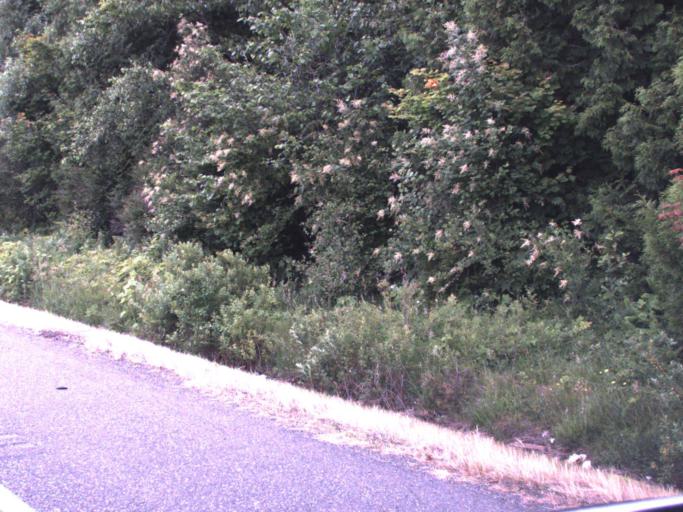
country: US
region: Washington
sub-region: Whatcom County
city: Birch Bay
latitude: 48.8921
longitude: -122.6911
